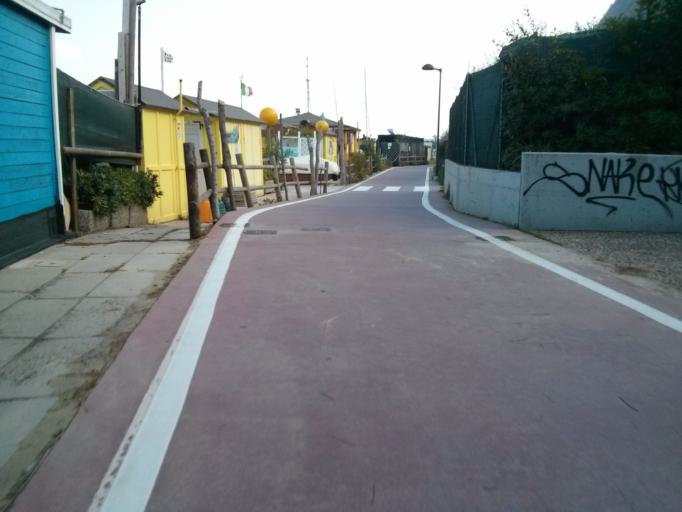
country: IT
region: The Marches
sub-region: Provincia di Pesaro e Urbino
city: Pesaro
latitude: 43.9025
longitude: 12.9341
